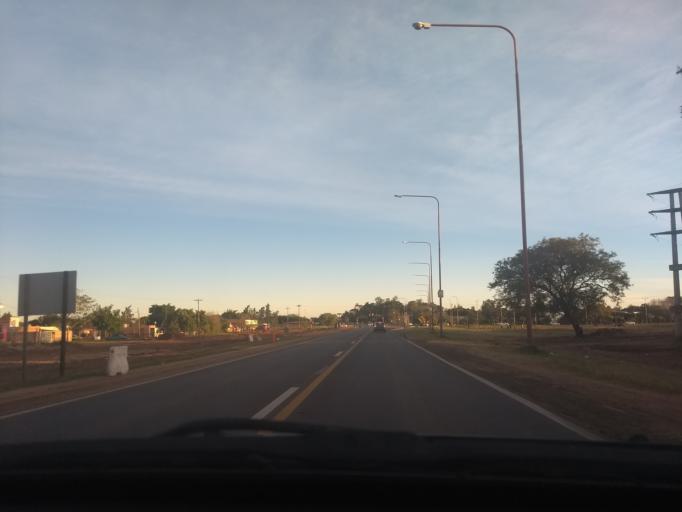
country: AR
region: Corrientes
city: Corrientes
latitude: -27.4761
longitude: -58.7824
